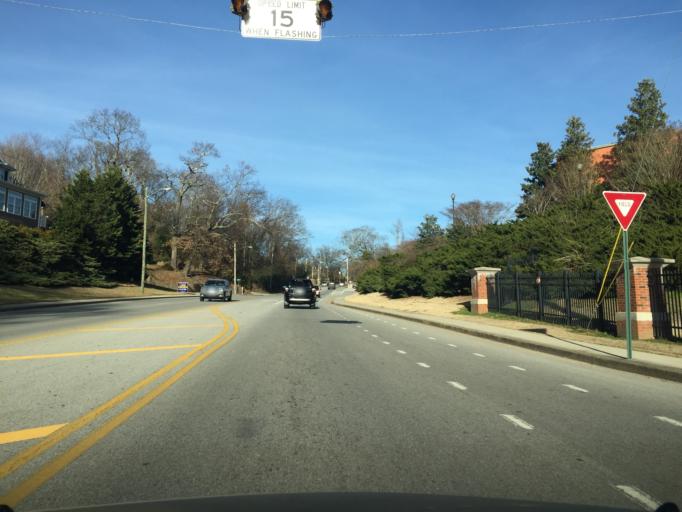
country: US
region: Tennessee
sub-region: Hamilton County
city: Chattanooga
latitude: 35.0624
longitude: -85.2997
